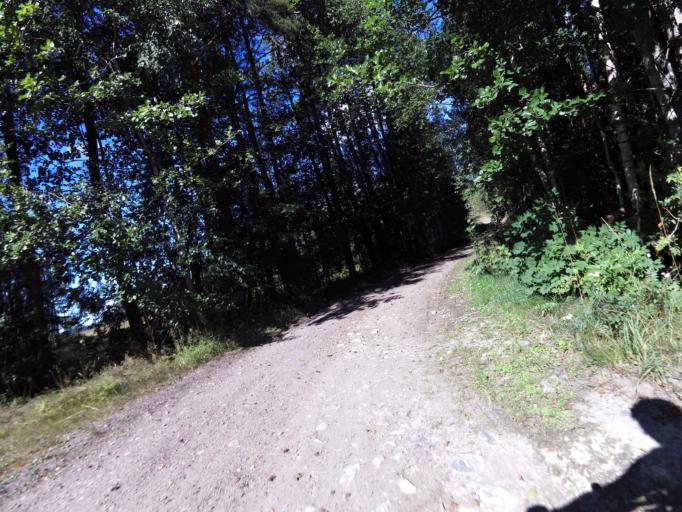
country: SE
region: Gaevleborg
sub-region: Gavle Kommun
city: Valbo
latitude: 60.7508
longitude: 16.9764
